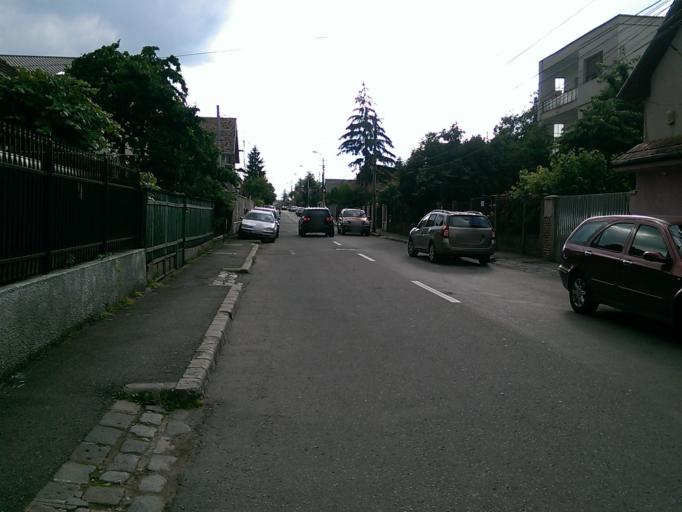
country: RO
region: Cluj
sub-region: Municipiul Cluj-Napoca
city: Cluj-Napoca
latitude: 46.7677
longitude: 23.6162
